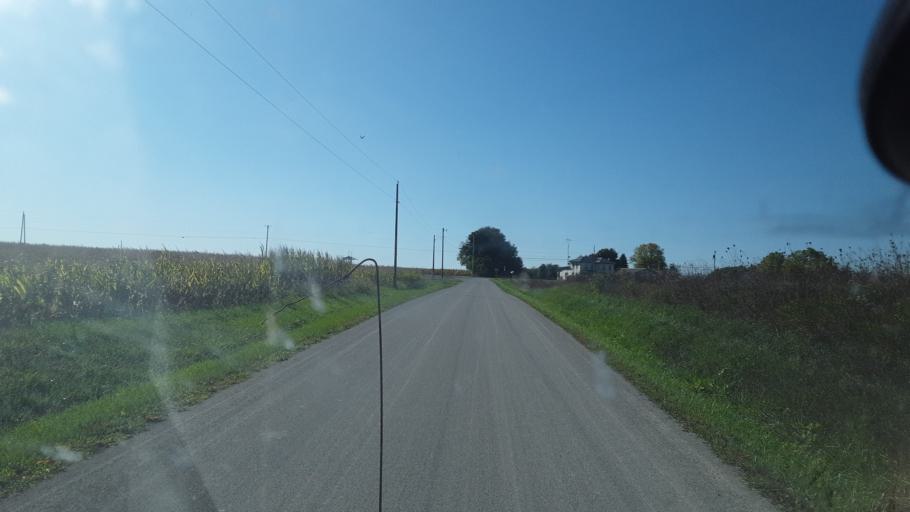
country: US
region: Ohio
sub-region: Hardin County
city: Forest
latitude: 40.7090
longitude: -83.4452
